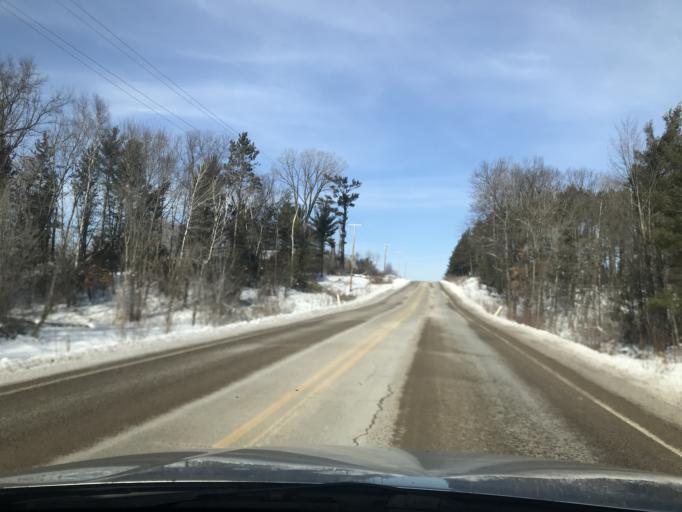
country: US
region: Wisconsin
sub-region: Oconto County
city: Oconto Falls
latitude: 45.1413
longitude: -88.1772
